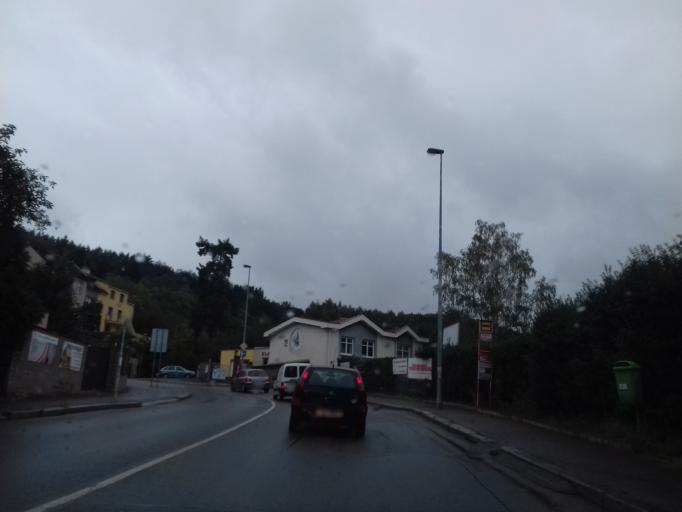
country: CZ
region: Praha
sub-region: Praha 1
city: Mala Strana
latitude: 50.0569
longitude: 14.3694
